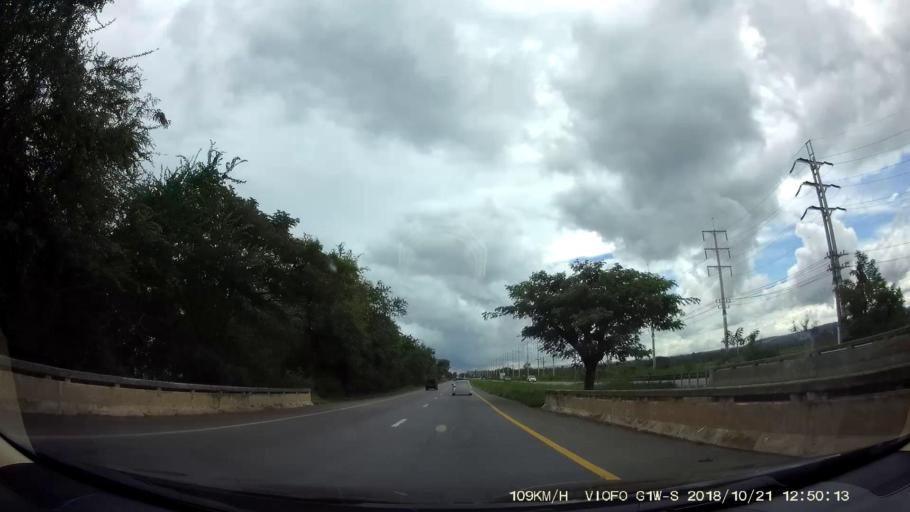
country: TH
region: Nakhon Ratchasima
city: Amphoe Sikhiu
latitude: 14.8854
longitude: 101.6888
